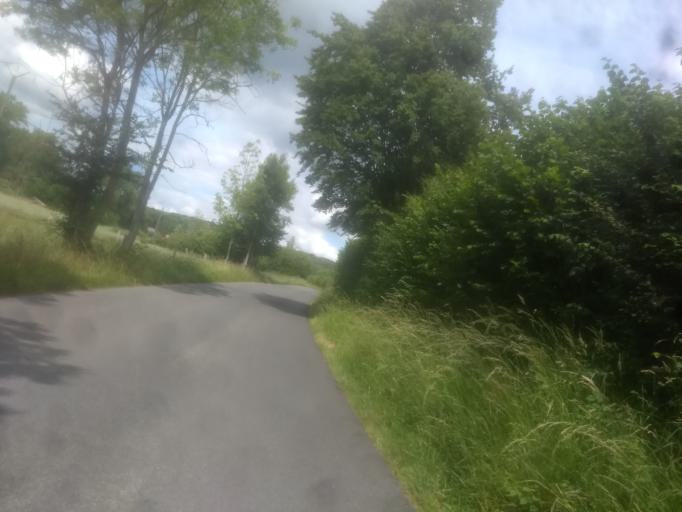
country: FR
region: Nord-Pas-de-Calais
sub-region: Departement du Pas-de-Calais
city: Maroeuil
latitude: 50.3324
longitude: 2.6888
